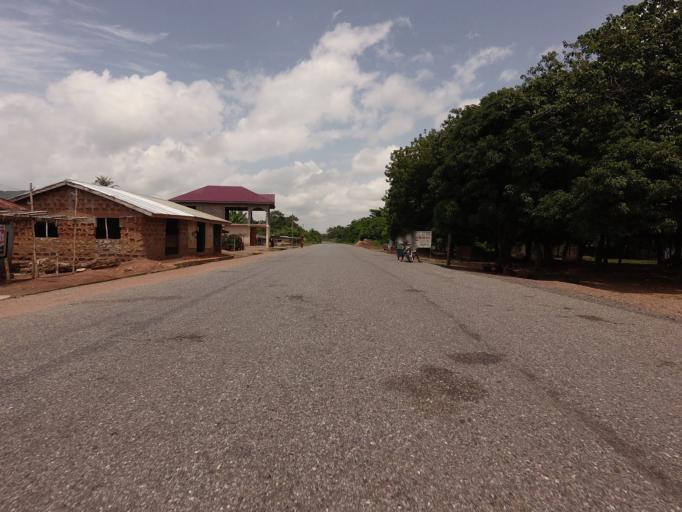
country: GH
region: Volta
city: Kpandu
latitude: 6.8629
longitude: 0.3979
